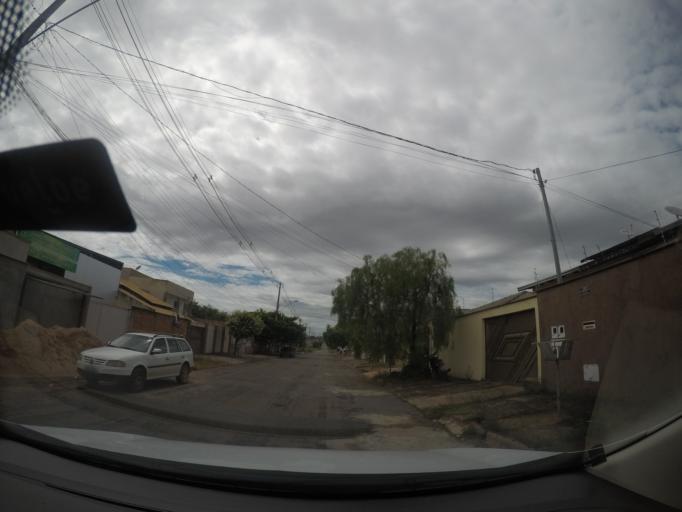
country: BR
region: Goias
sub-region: Goiania
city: Goiania
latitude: -16.7250
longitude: -49.3477
